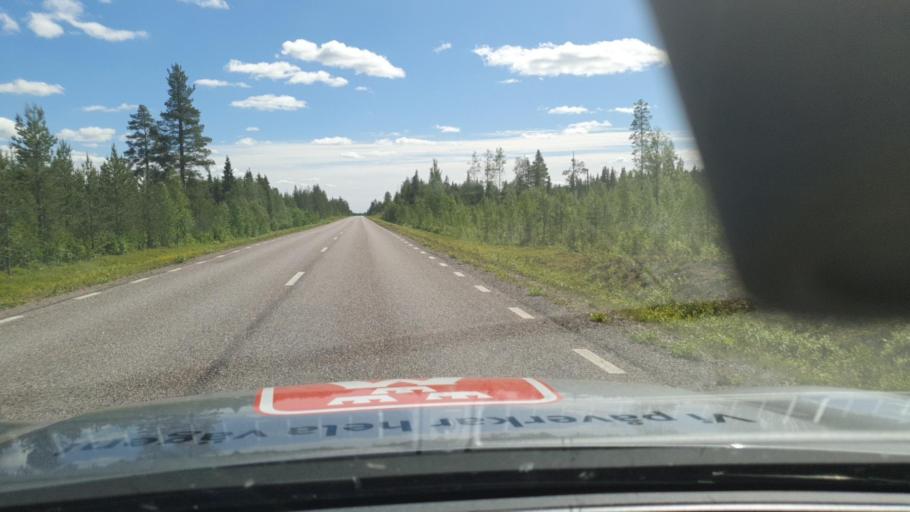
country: SE
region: Norrbotten
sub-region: Pajala Kommun
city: Pajala
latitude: 67.1545
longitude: 23.5541
